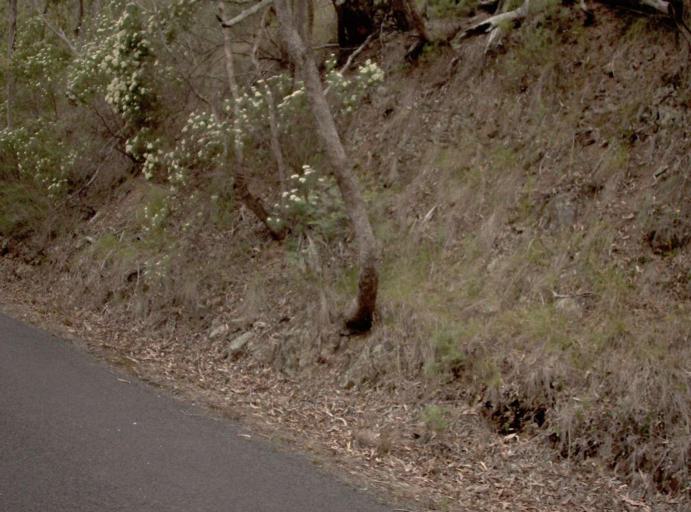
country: AU
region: Victoria
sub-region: East Gippsland
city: Bairnsdale
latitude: -37.4880
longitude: 147.2047
